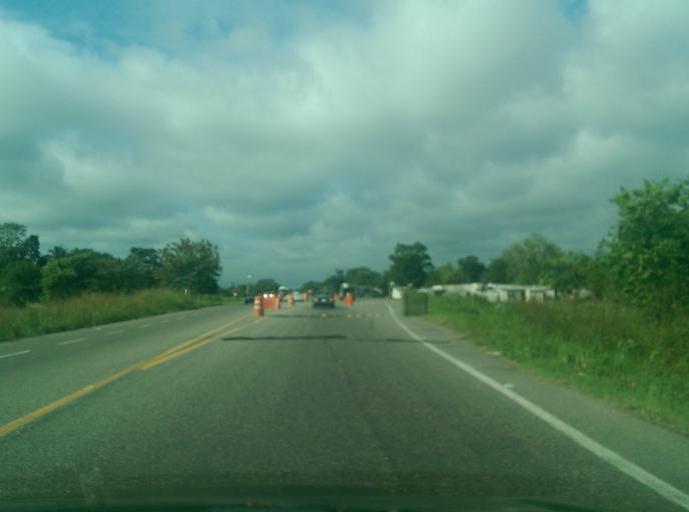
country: MX
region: Tabasco
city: Aquiles Serdan
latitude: 17.6933
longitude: -92.3139
